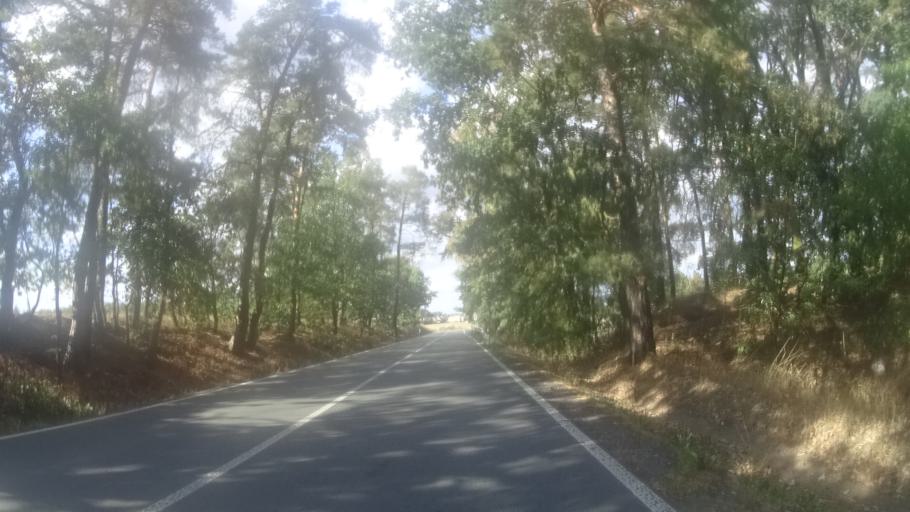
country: CZ
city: Albrechtice nad Orlici
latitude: 50.1349
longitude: 16.0585
